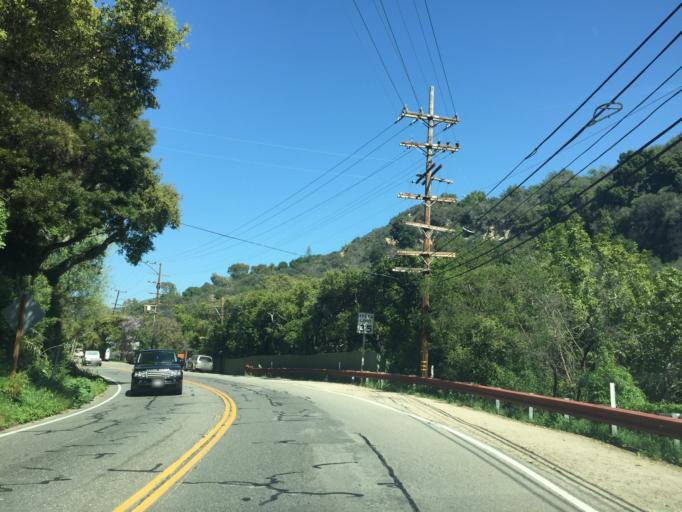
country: US
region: California
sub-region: Los Angeles County
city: Topanga
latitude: 34.0850
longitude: -118.6000
